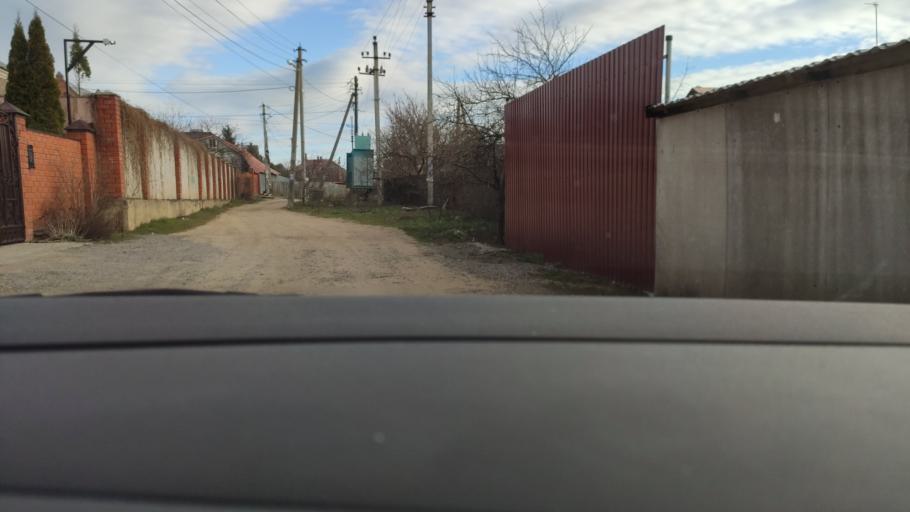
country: RU
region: Voronezj
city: Pridonskoy
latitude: 51.6575
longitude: 39.0911
